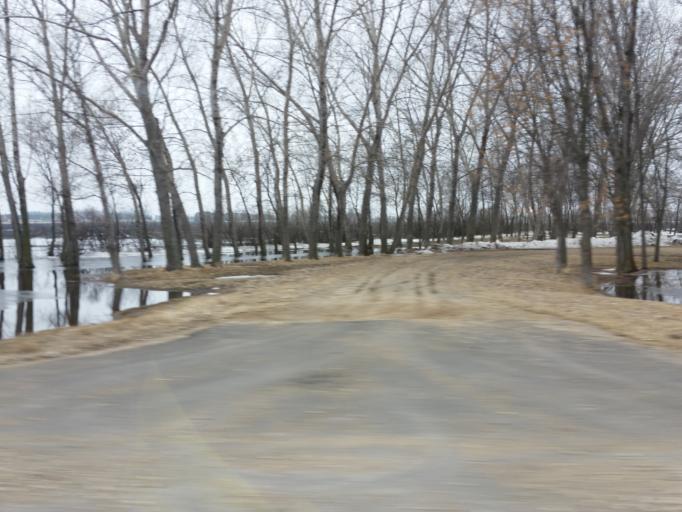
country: US
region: North Dakota
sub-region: Walsh County
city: Grafton
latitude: 48.6052
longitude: -97.4478
